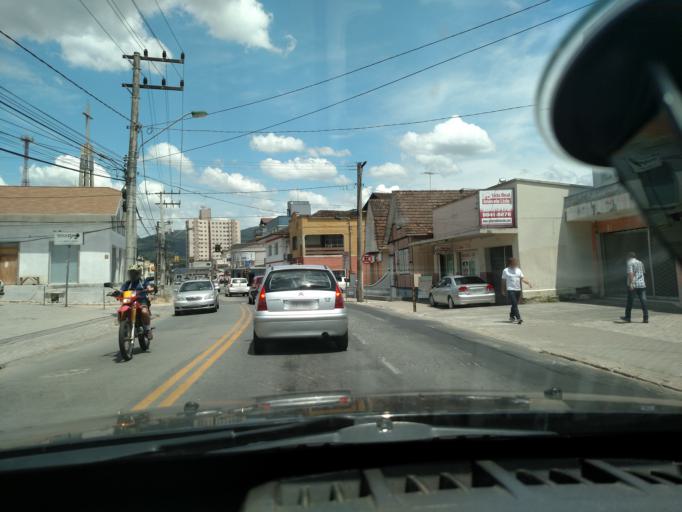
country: BR
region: Santa Catarina
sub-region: Blumenau
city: Blumenau
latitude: -26.9501
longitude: -49.0721
